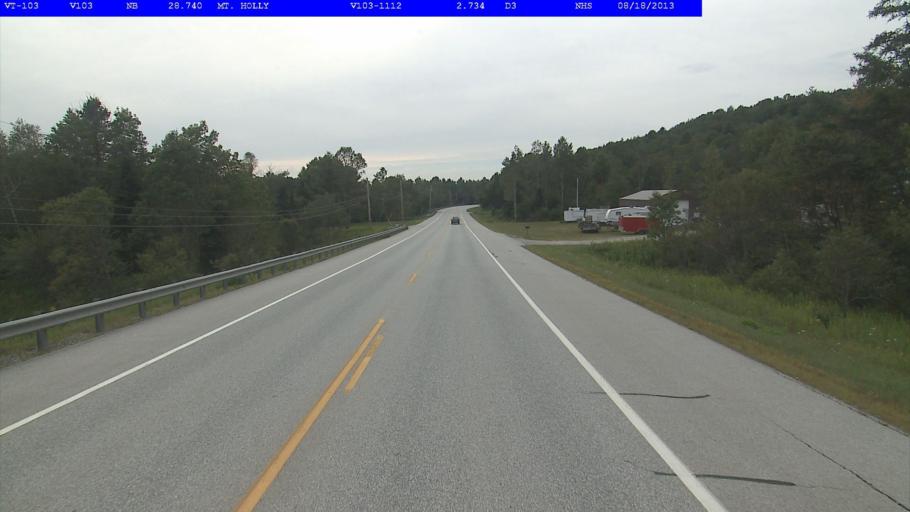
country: US
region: Vermont
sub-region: Rutland County
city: Rutland
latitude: 43.4495
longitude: -72.7813
